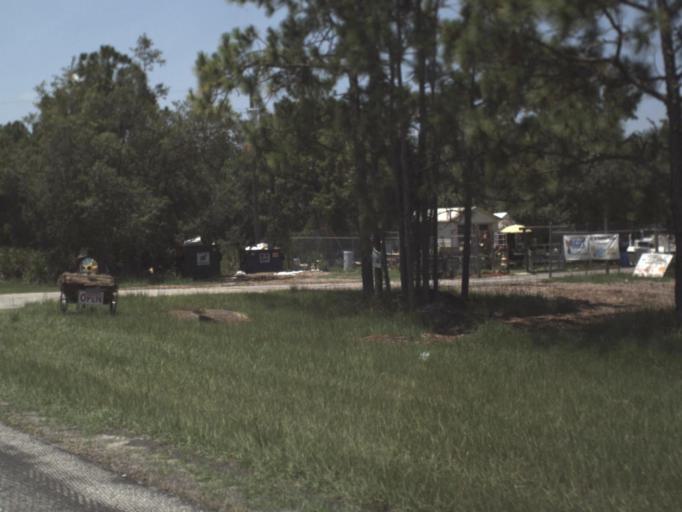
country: US
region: Florida
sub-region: Citrus County
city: Sugarmill Woods
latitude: 28.6545
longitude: -82.5523
